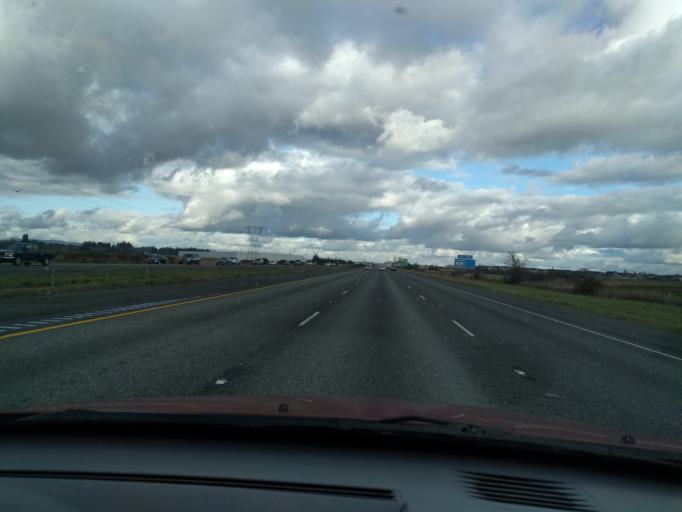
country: US
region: Oregon
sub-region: Marion County
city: Gervais
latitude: 45.1354
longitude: -122.8965
